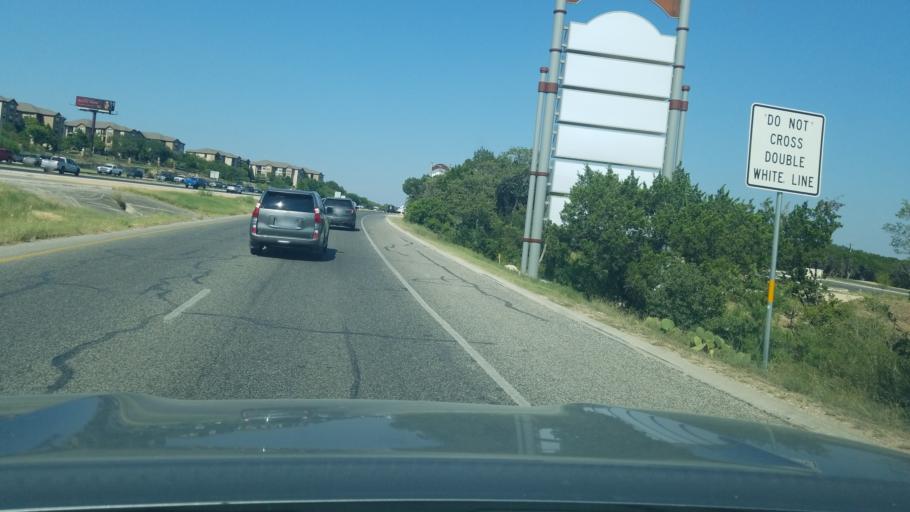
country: US
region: Texas
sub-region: Bexar County
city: Shavano Park
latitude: 29.6000
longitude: -98.5616
